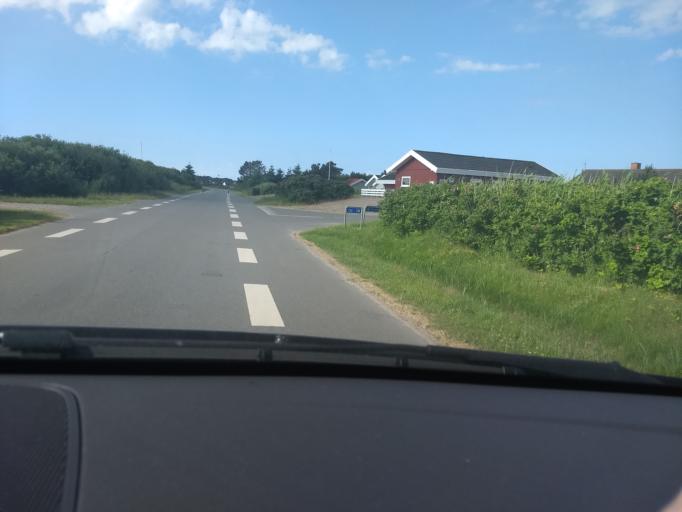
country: DE
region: Schleswig-Holstein
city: List
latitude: 55.1390
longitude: 8.4942
